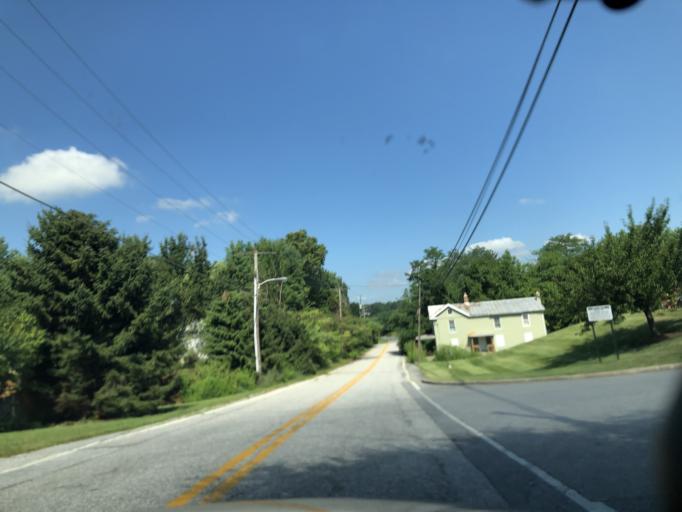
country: US
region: Maryland
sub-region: Carroll County
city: Westminster
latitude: 39.5855
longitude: -77.0138
